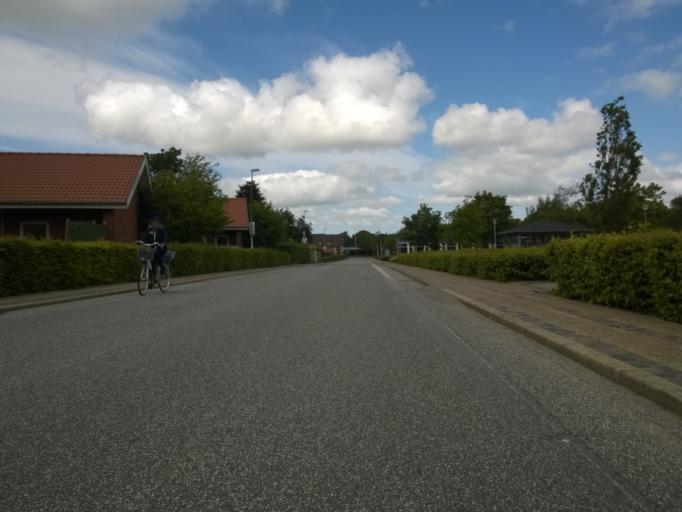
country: DK
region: Central Jutland
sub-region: Holstebro Kommune
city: Vinderup
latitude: 56.4770
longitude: 8.7829
